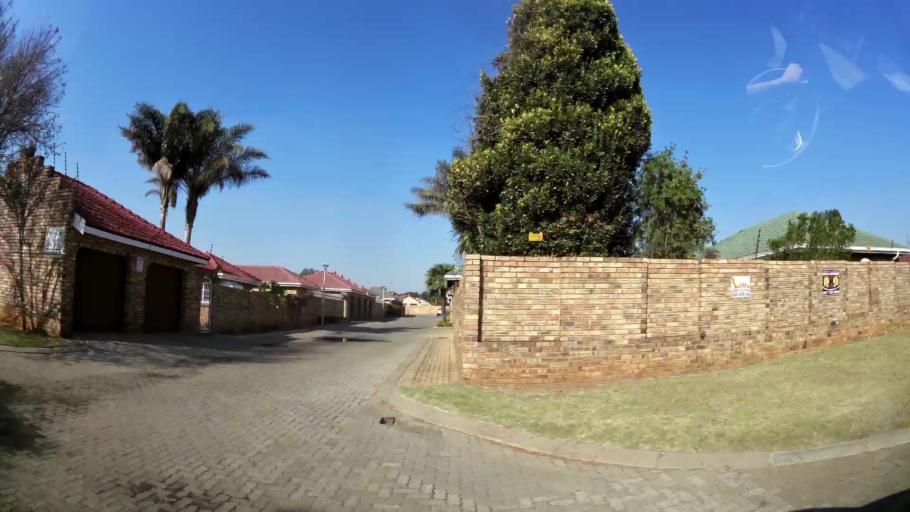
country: ZA
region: Gauteng
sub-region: West Rand District Municipality
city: Randfontein
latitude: -26.1780
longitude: 27.6915
